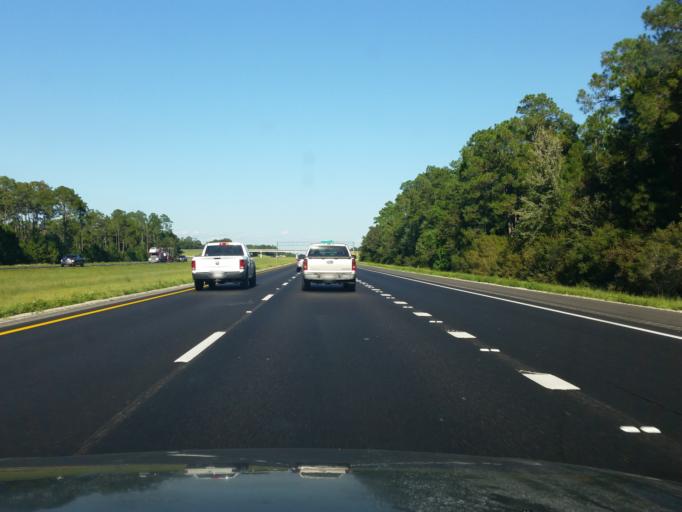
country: US
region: Mississippi
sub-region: Hancock County
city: Diamondhead
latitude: 30.3702
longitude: -89.3841
